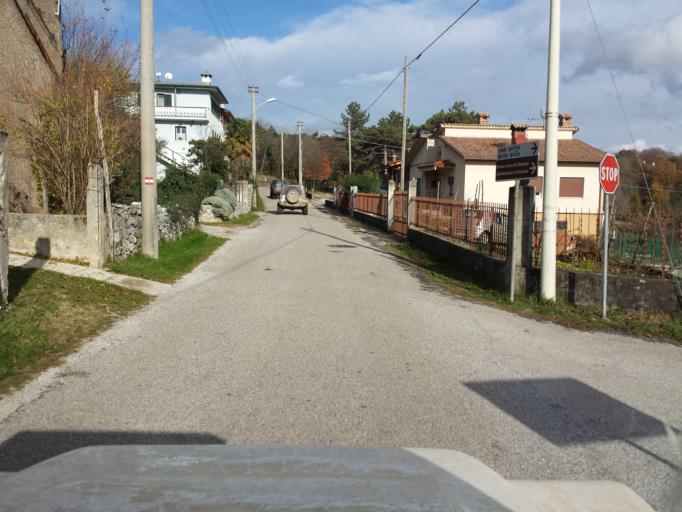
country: IT
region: Friuli Venezia Giulia
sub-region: Provincia di Gorizia
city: Savogna d'Isonzo
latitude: 45.8805
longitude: 13.5593
